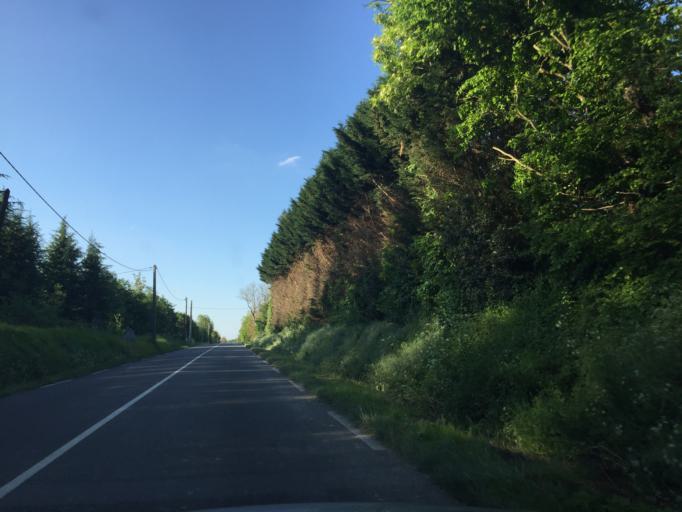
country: FR
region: Poitou-Charentes
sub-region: Departement de la Charente
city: Chalais
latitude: 45.2115
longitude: 0.0323
